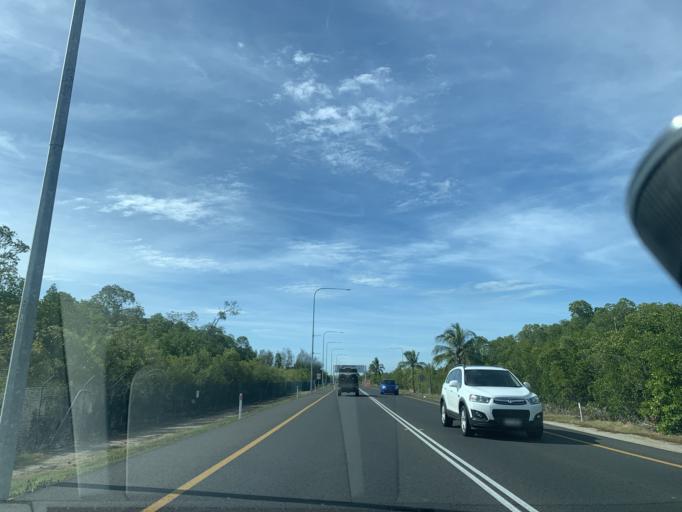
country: AU
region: Queensland
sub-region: Cairns
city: Cairns
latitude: -16.8856
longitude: 145.7619
